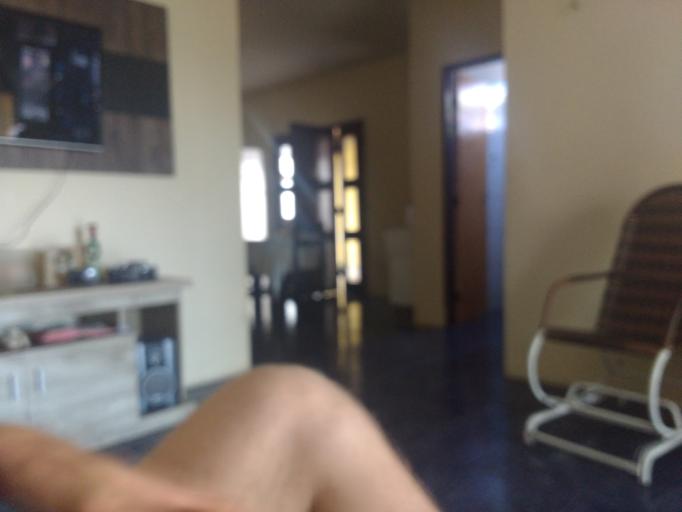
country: BR
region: Ceara
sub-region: Fortaleza
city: Fortaleza
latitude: -3.7322
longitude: -38.5720
